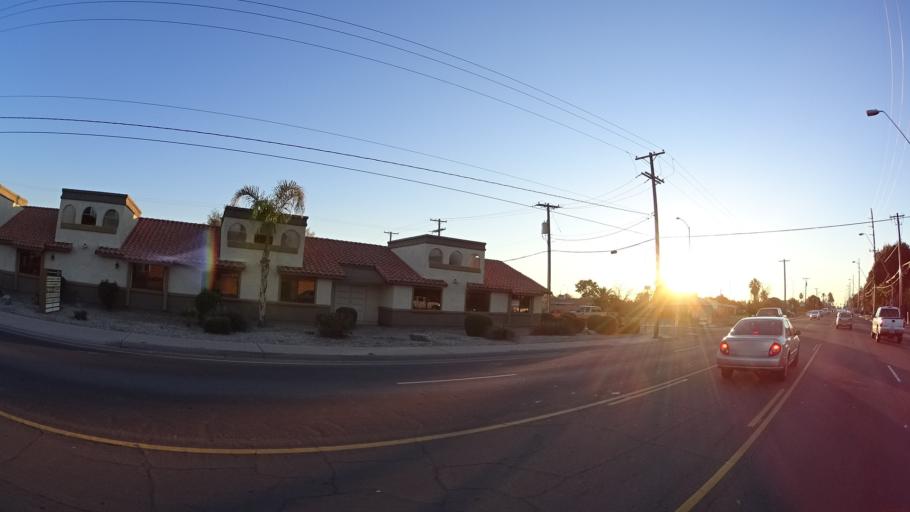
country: US
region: Arizona
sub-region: Maricopa County
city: Mesa
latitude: 33.4224
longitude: -111.8436
